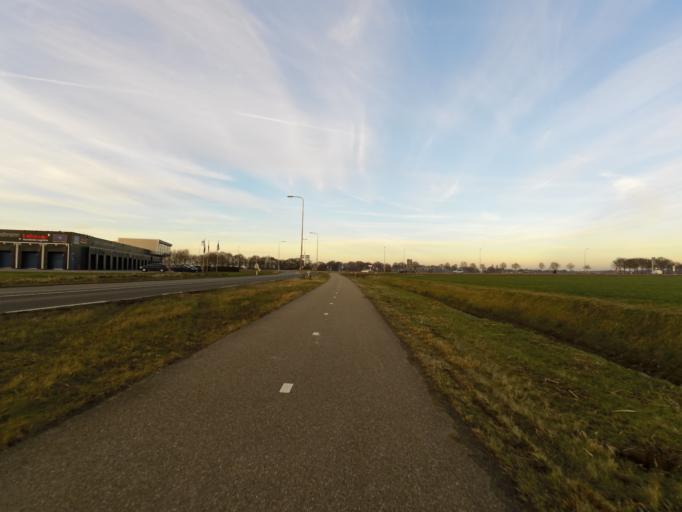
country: NL
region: Gelderland
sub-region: Gemeente Montferland
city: s-Heerenberg
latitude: 51.8778
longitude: 6.2766
